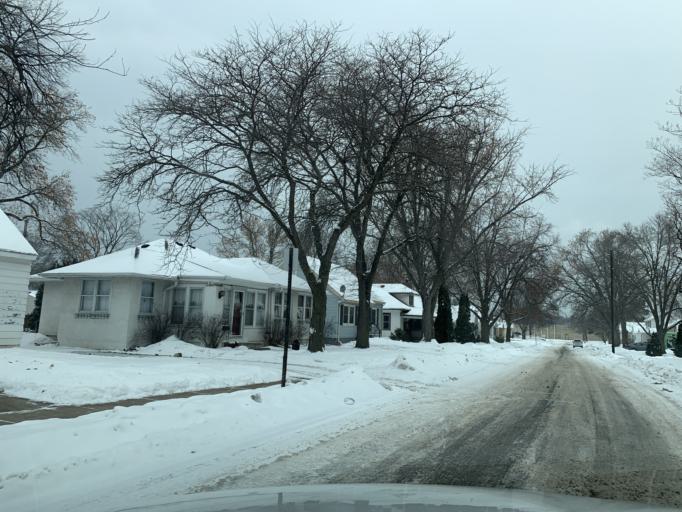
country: US
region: Minnesota
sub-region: Hennepin County
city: Saint Louis Park
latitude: 44.9268
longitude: -93.3509
